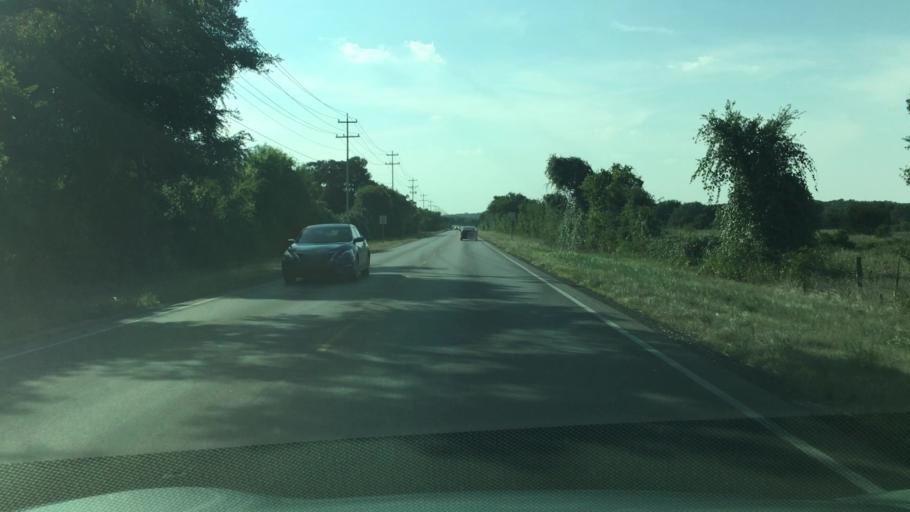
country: US
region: Texas
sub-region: Travis County
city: Shady Hollow
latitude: 30.1077
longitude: -97.9444
